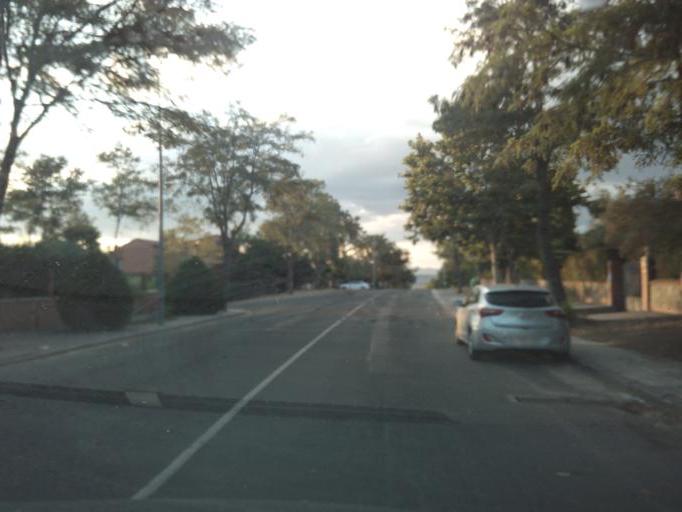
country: ES
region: Madrid
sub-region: Provincia de Madrid
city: Valdeolmos
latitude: 40.6133
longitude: -3.4702
